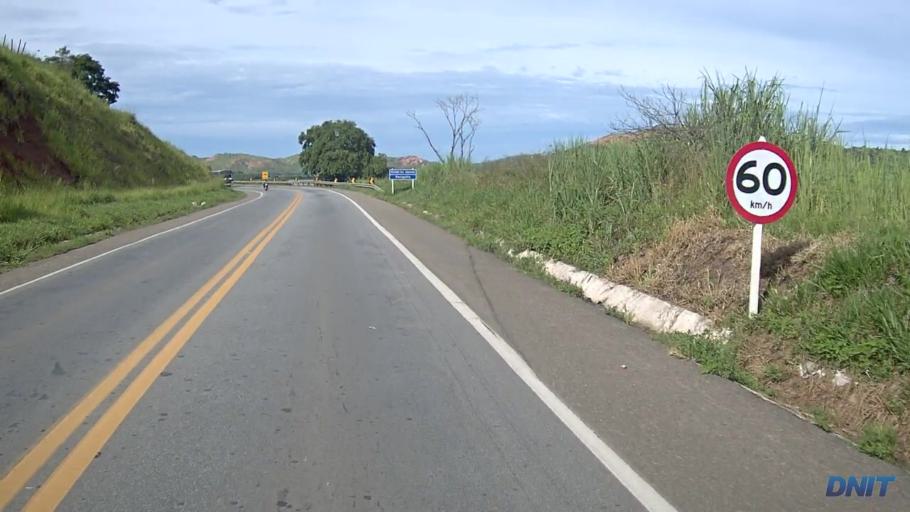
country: BR
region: Minas Gerais
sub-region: Belo Oriente
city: Belo Oriente
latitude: -19.1606
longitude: -42.2394
